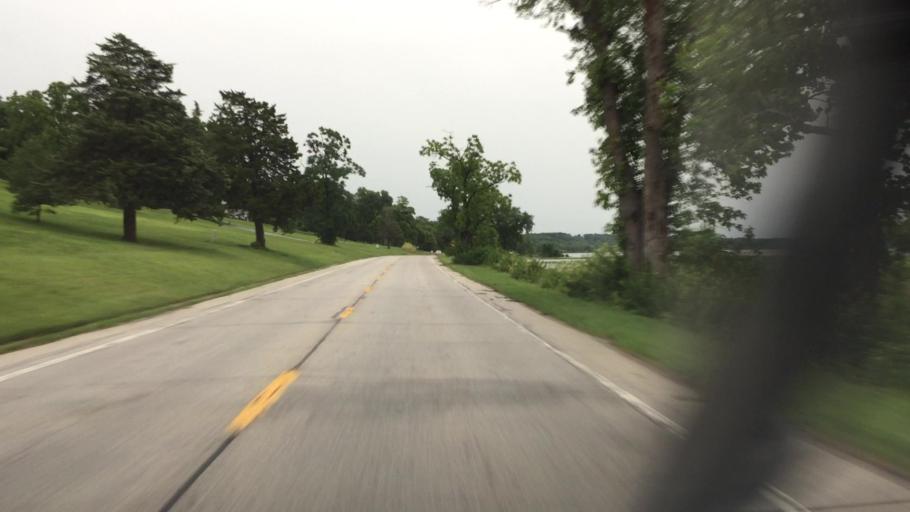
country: US
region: Illinois
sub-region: Hancock County
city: Nauvoo
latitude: 40.5288
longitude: -91.3712
